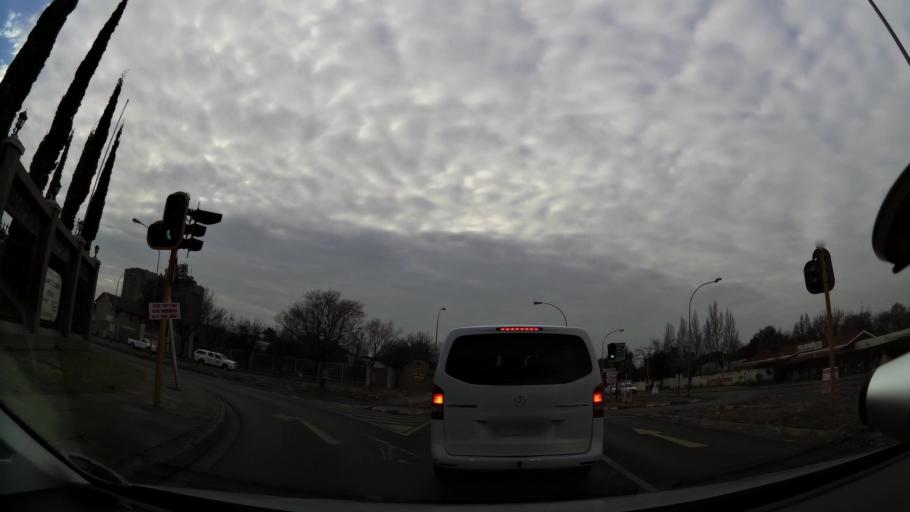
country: ZA
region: Orange Free State
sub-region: Mangaung Metropolitan Municipality
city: Bloemfontein
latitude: -29.1188
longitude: 26.1816
